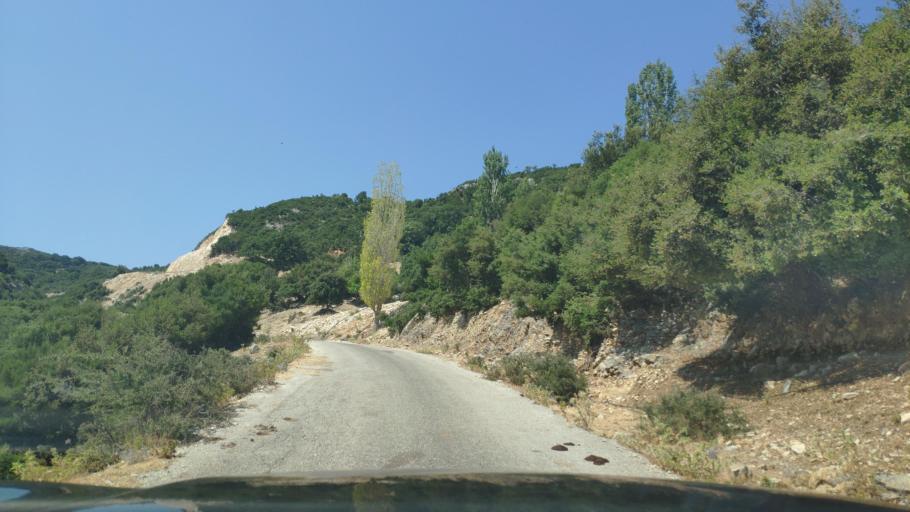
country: GR
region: West Greece
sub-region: Nomos Aitolias kai Akarnanias
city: Monastirakion
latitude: 38.8317
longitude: 20.9314
